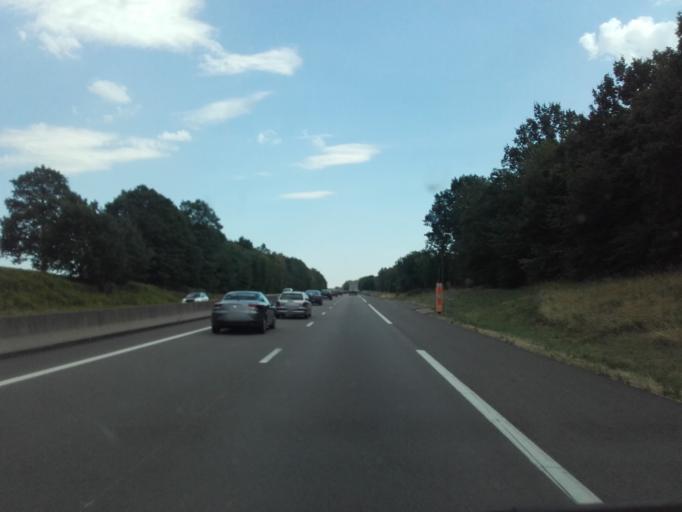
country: FR
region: Bourgogne
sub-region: Departement de la Cote-d'Or
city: Semur-en-Auxois
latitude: 47.4588
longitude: 4.2571
